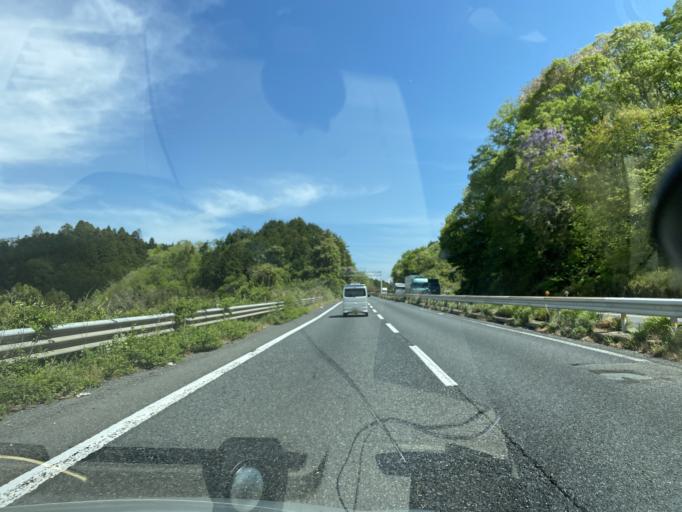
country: JP
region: Mie
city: Nabari
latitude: 34.6656
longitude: 136.0328
